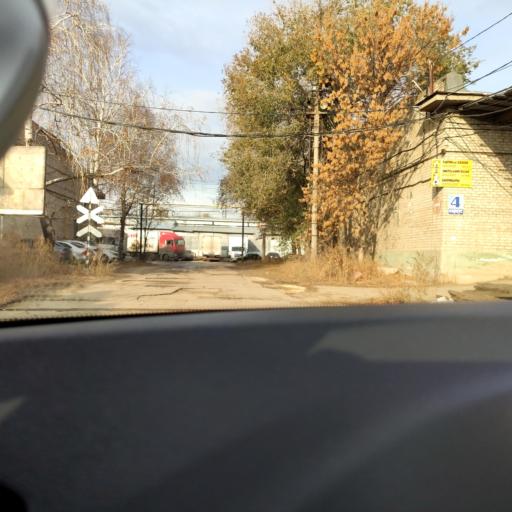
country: RU
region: Samara
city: Petra-Dubrava
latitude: 53.2461
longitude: 50.2999
